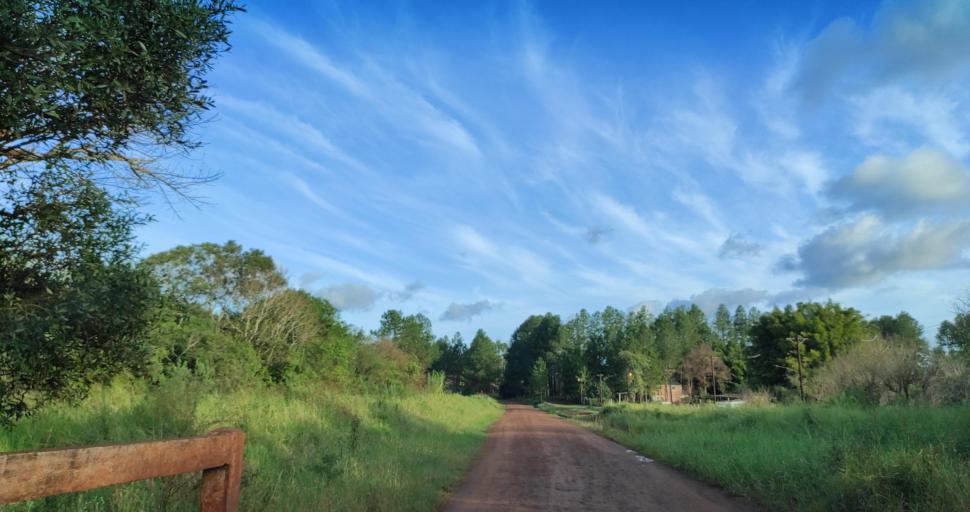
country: AR
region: Misiones
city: Garupa
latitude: -27.5094
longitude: -55.8547
